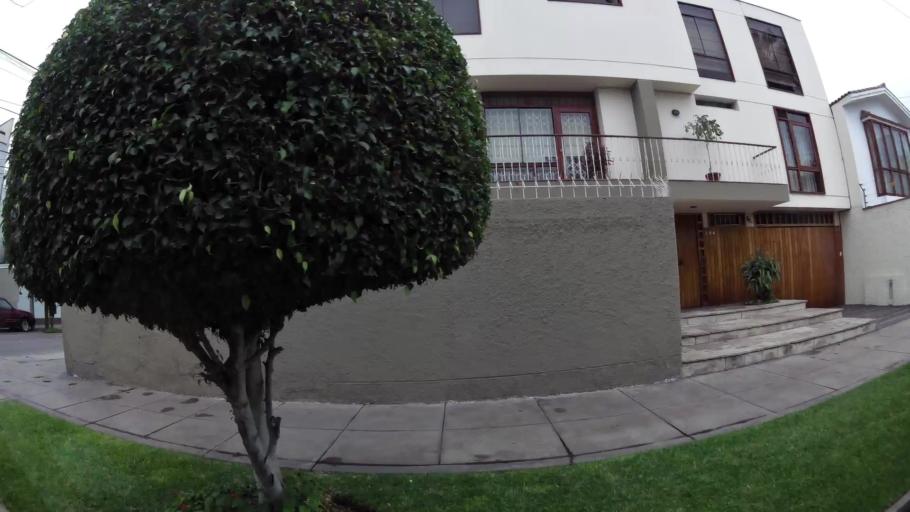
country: PE
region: Lima
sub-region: Lima
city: Surco
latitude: -12.1294
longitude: -77.0147
